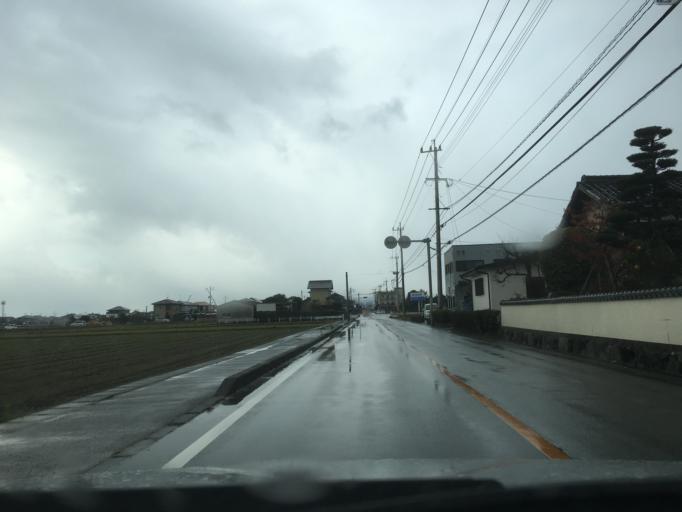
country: JP
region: Saga Prefecture
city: Tosu
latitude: 33.3778
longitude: 130.5658
